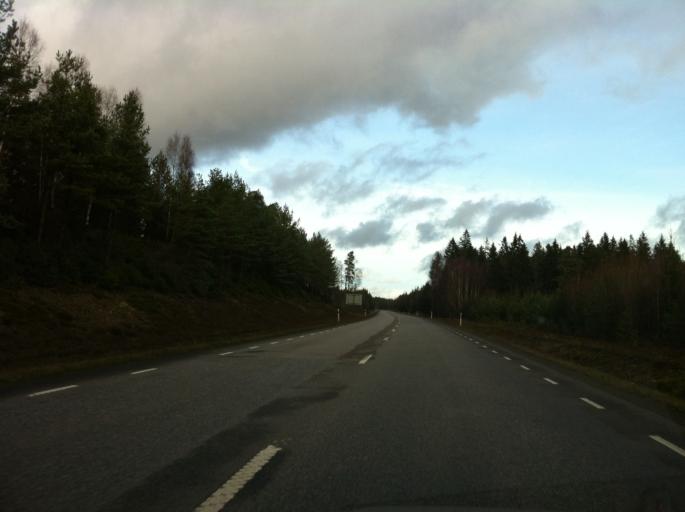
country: SE
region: Kronoberg
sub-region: Almhults Kommun
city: AElmhult
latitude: 56.5494
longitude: 14.1642
